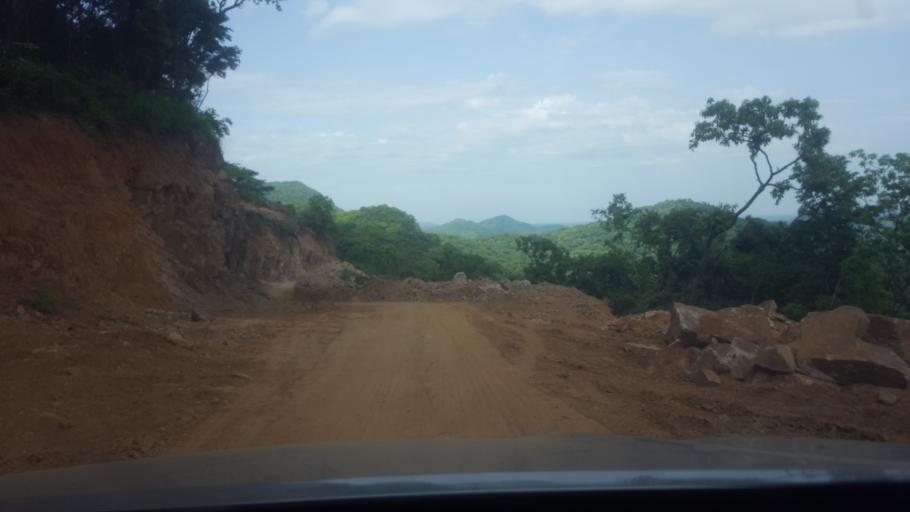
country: ET
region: Southern Nations, Nationalities, and People's Region
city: Tippi
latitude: 7.5384
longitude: 34.9741
